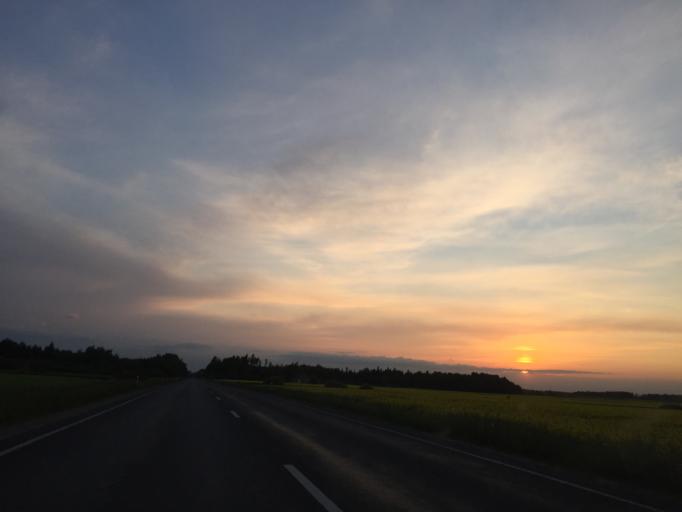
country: LT
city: Kursenai
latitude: 55.9979
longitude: 22.8473
